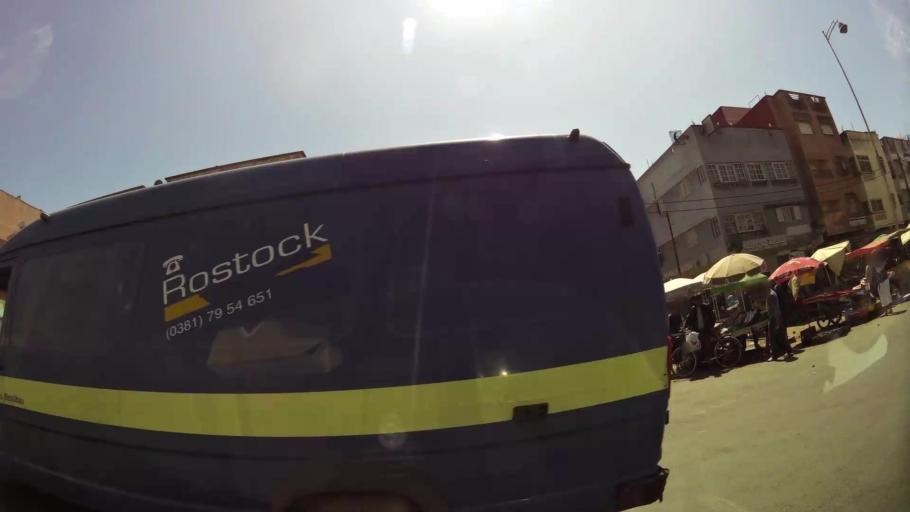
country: MA
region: Gharb-Chrarda-Beni Hssen
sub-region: Kenitra Province
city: Kenitra
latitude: 34.2439
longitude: -6.5509
